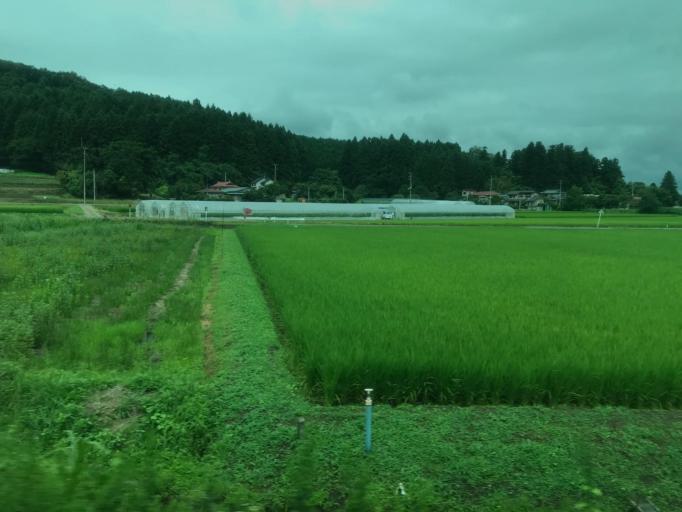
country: JP
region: Fukushima
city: Ishikawa
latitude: 37.1527
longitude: 140.2944
